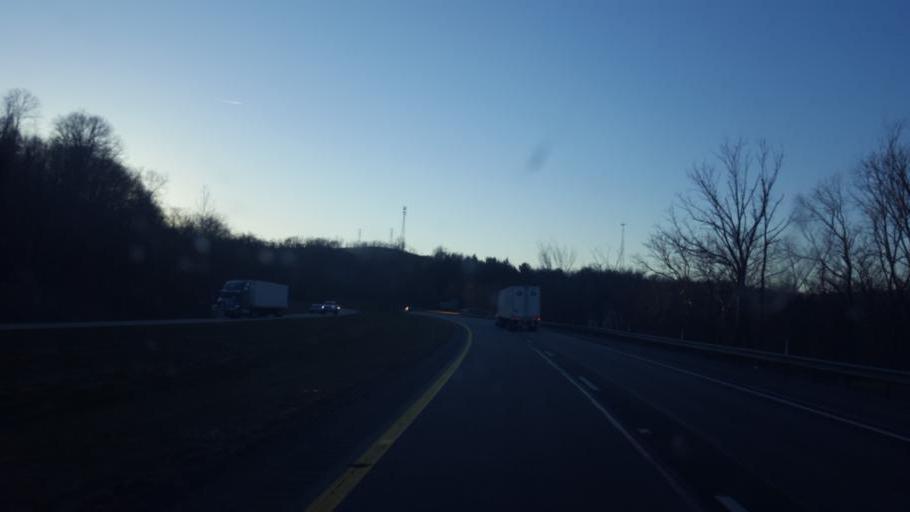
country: US
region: West Virginia
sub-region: Brooke County
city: Bethany
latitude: 40.1184
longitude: -80.4716
